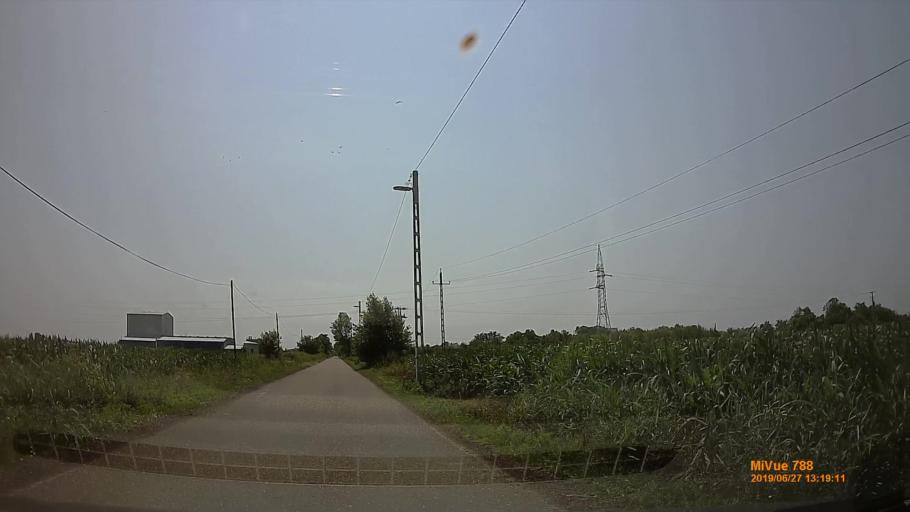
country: HU
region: Pest
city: Cegled
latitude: 47.1894
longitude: 19.8254
